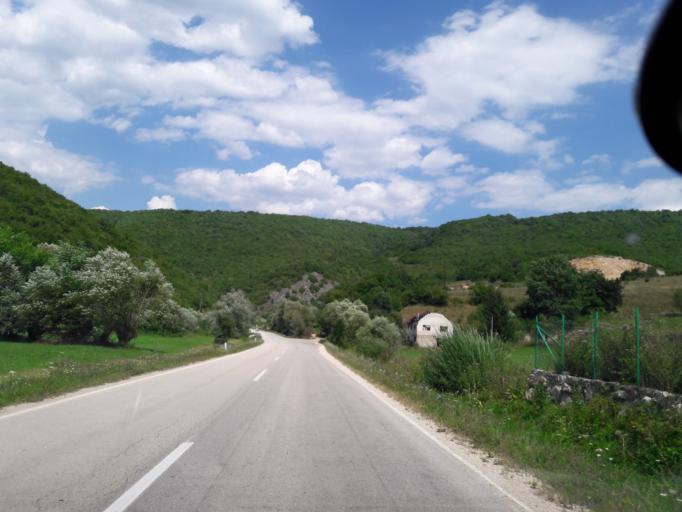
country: BA
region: Republika Srpska
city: Mrkonjic Grad
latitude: 44.4425
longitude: 17.1608
